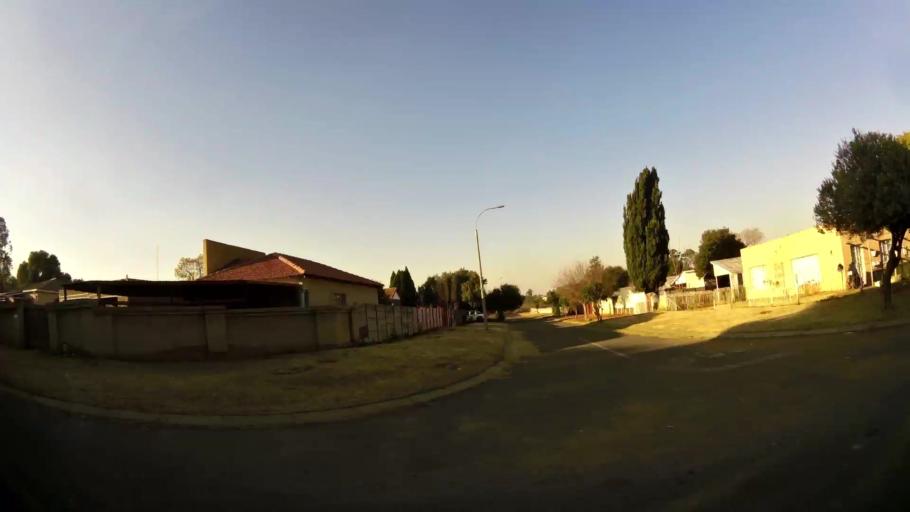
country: ZA
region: Gauteng
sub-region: West Rand District Municipality
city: Randfontein
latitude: -26.2245
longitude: 27.6462
